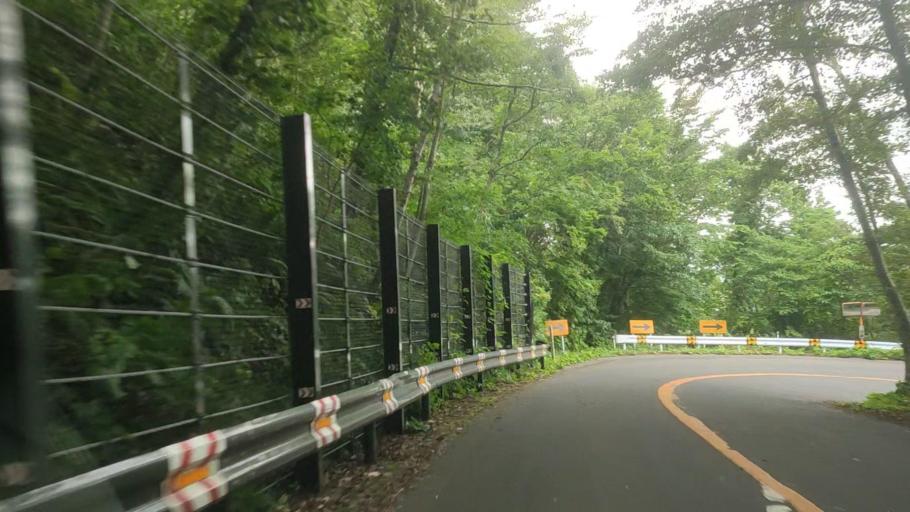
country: JP
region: Hokkaido
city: Hakodate
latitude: 41.7627
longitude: 140.7010
